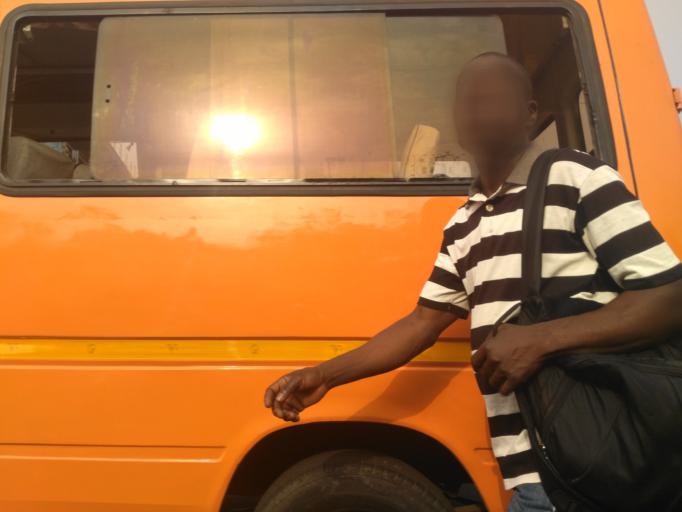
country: GH
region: Greater Accra
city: Accra
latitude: 5.5483
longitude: -0.2104
